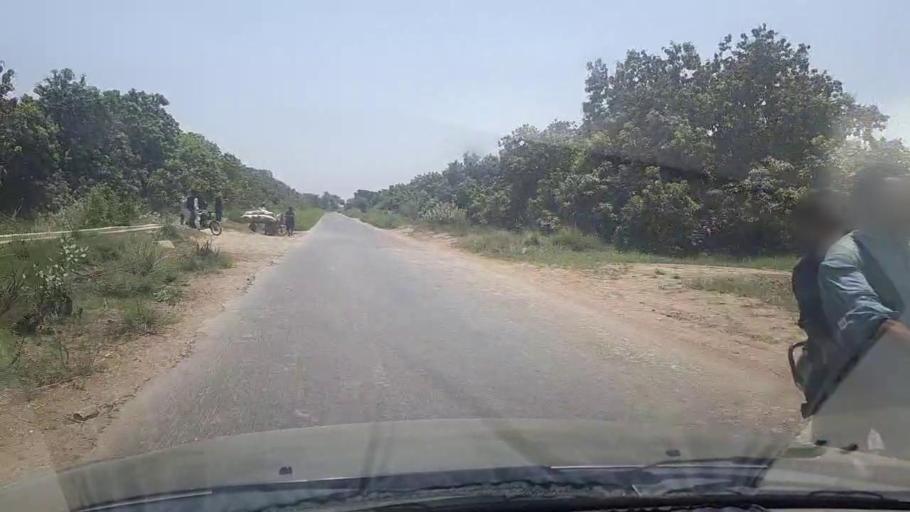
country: PK
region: Sindh
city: Tando Jam
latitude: 25.2855
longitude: 68.5970
